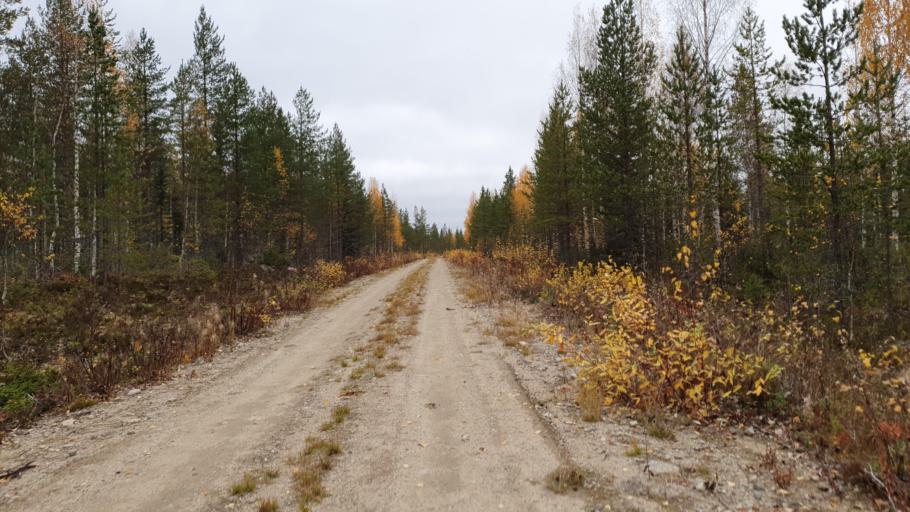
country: FI
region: Kainuu
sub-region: Kehys-Kainuu
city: Kuhmo
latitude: 64.4409
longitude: 29.6186
